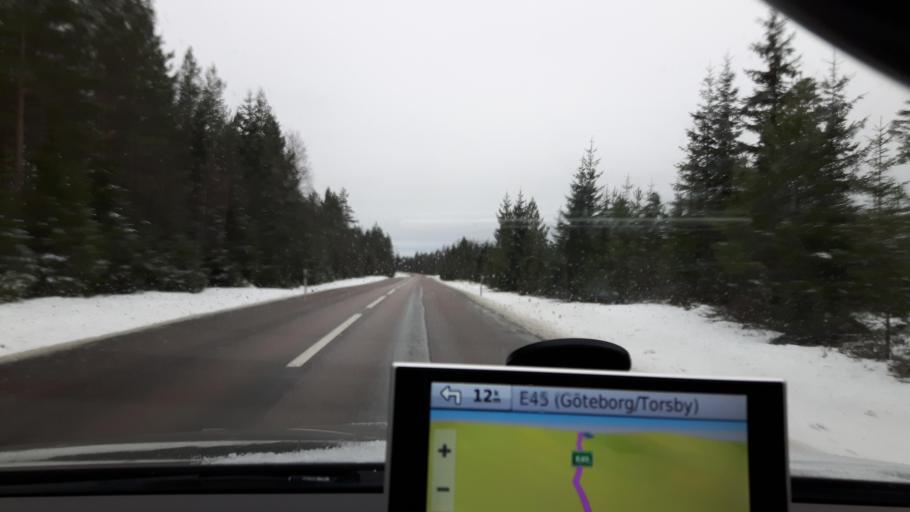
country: SE
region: Vaermland
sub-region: Torsby Kommun
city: Torsby
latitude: 60.3599
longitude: 13.1805
